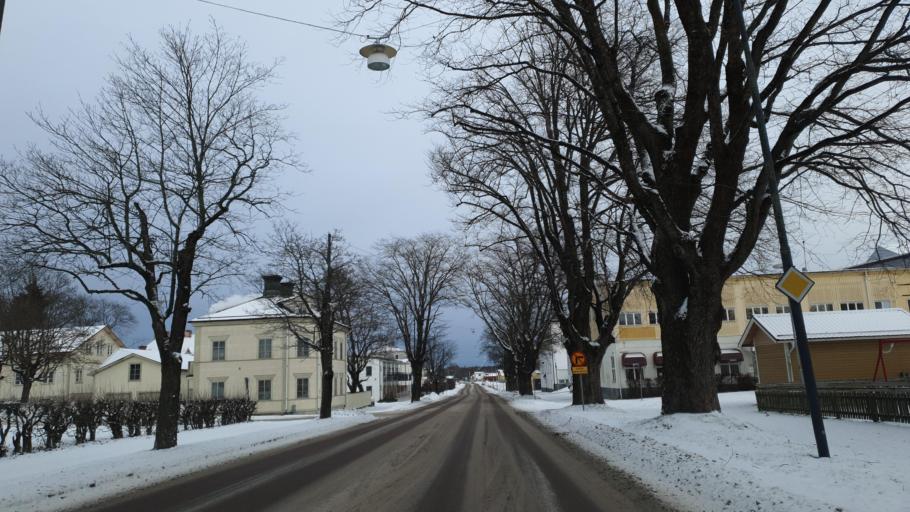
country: SE
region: Gaevleborg
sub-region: Soderhamns Kommun
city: Soderhamn
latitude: 61.3069
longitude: 17.0648
